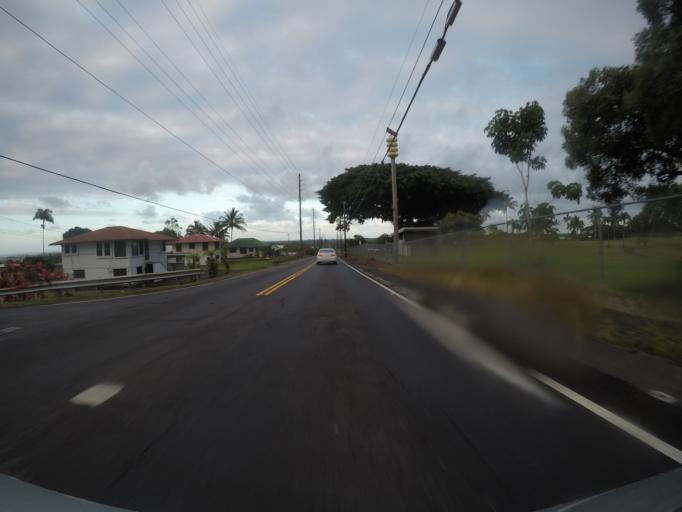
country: US
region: Hawaii
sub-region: Hawaii County
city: Hilo
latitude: 19.6839
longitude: -155.0791
